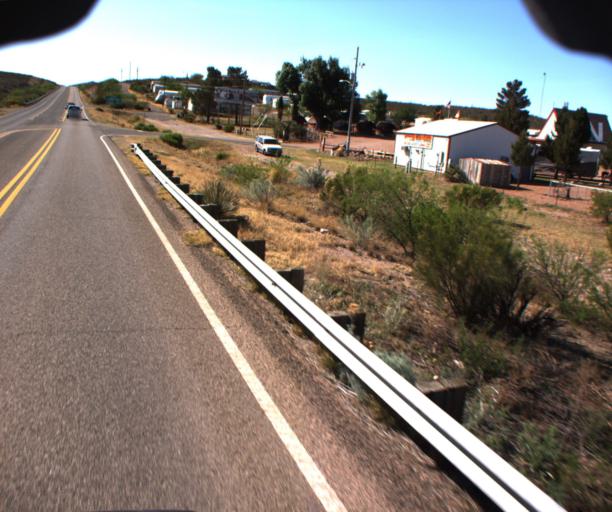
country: US
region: Arizona
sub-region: Cochise County
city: Tombstone
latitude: 31.7312
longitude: -110.0799
